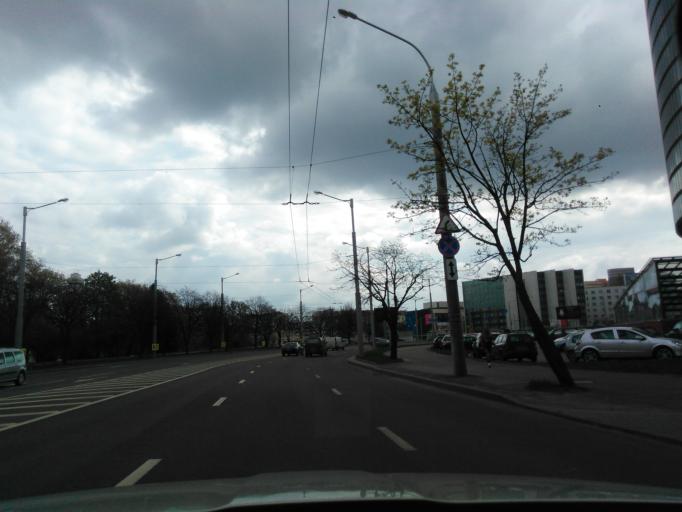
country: BY
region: Minsk
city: Minsk
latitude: 53.9077
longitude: 27.5324
